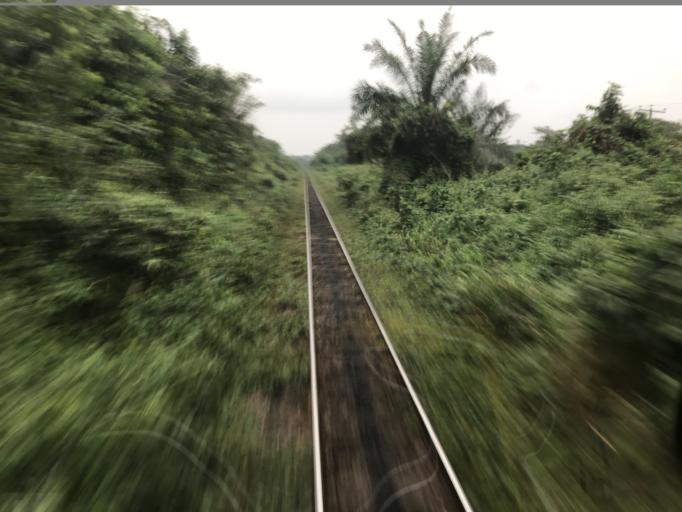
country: CM
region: Littoral
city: Edea
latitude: 3.9186
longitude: 10.1073
